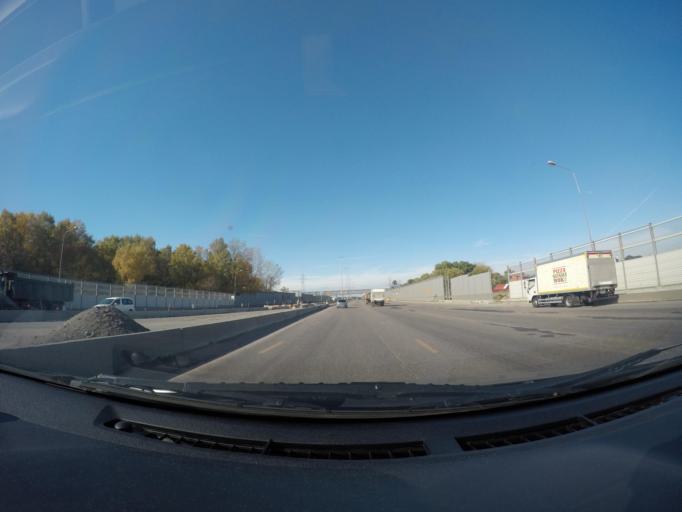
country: RU
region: Moskovskaya
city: Tomilino
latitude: 55.6314
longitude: 37.9383
